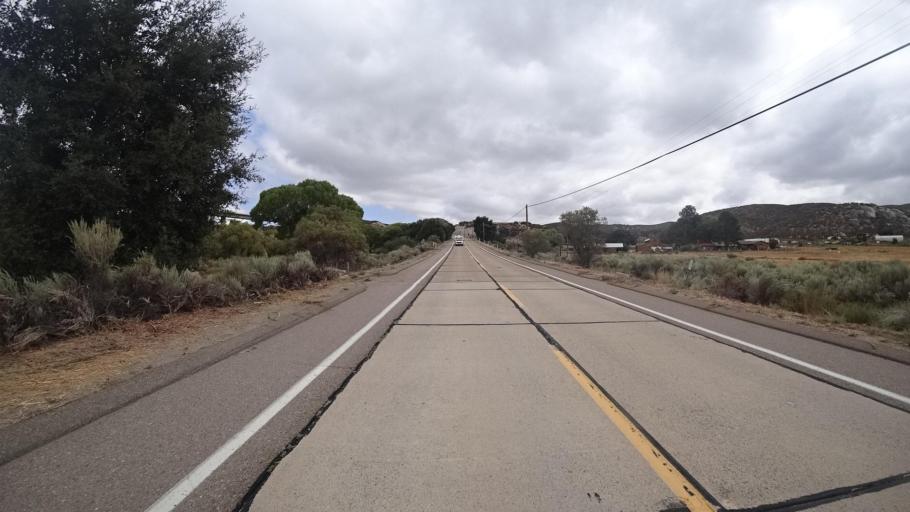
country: US
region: California
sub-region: San Diego County
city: Campo
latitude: 32.7242
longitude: -116.4299
